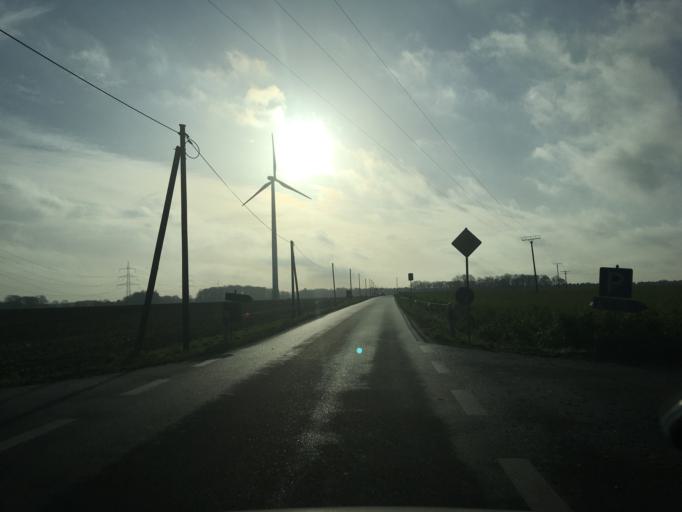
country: DE
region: North Rhine-Westphalia
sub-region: Regierungsbezirk Munster
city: Velen
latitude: 51.9299
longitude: 6.9636
